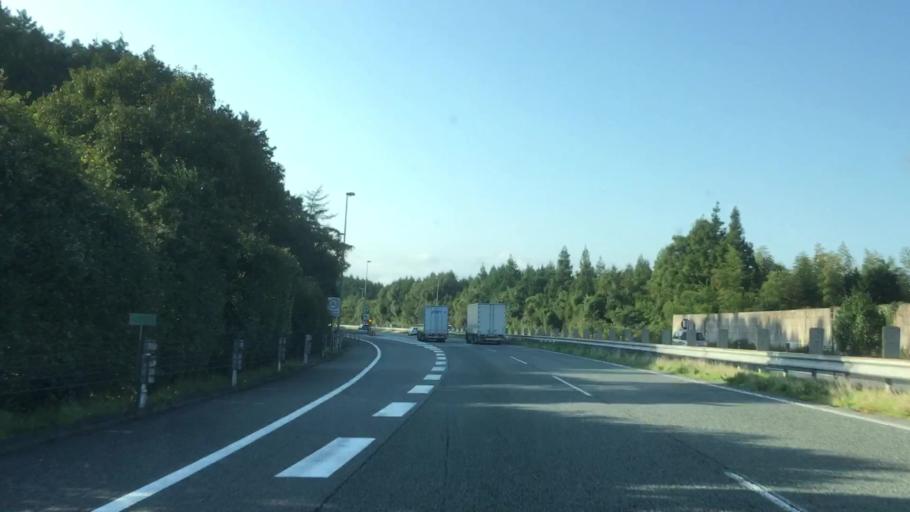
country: JP
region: Yamaguchi
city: Ogori-shimogo
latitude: 34.1509
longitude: 131.3417
